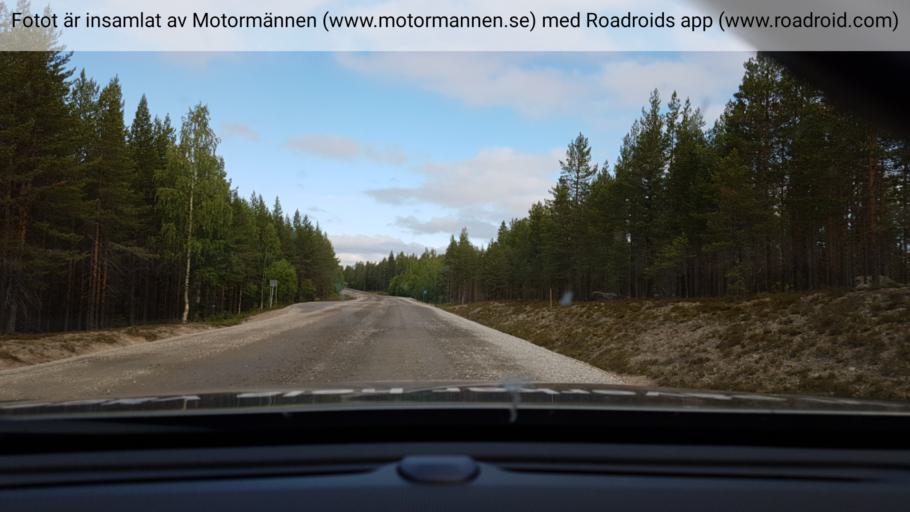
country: SE
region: Vaesterbotten
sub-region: Norsjo Kommun
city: Norsjoe
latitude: 64.6792
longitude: 19.2488
